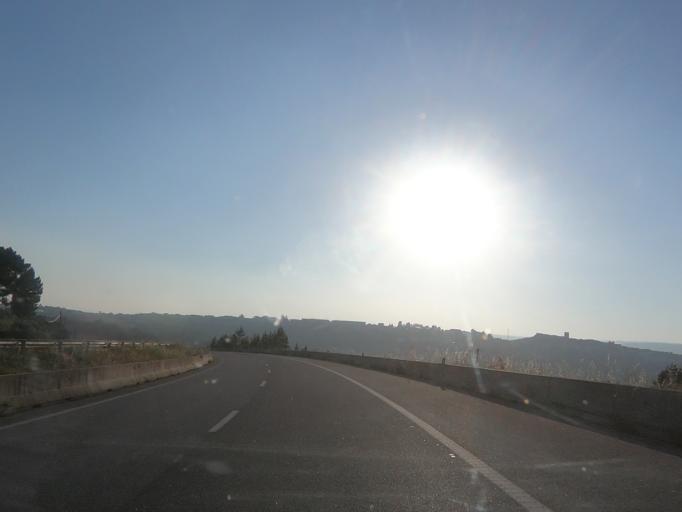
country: PT
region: Guarda
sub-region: Celorico da Beira
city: Celorico da Beira
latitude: 40.6278
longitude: -7.3718
